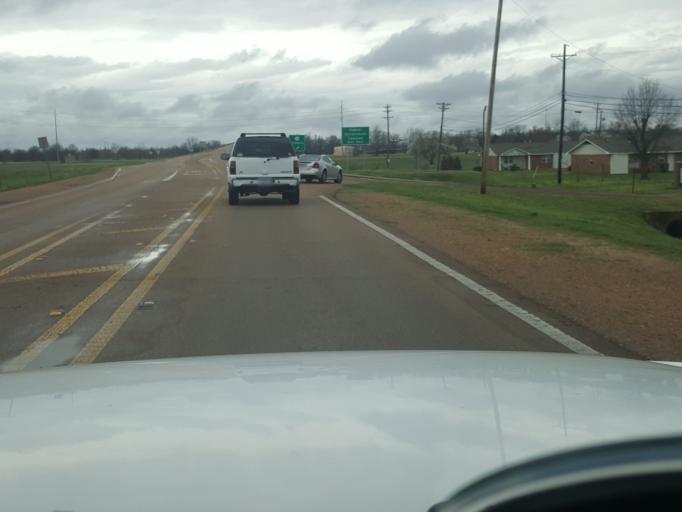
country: US
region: Mississippi
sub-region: Yazoo County
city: Yazoo City
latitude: 32.8523
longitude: -90.4255
